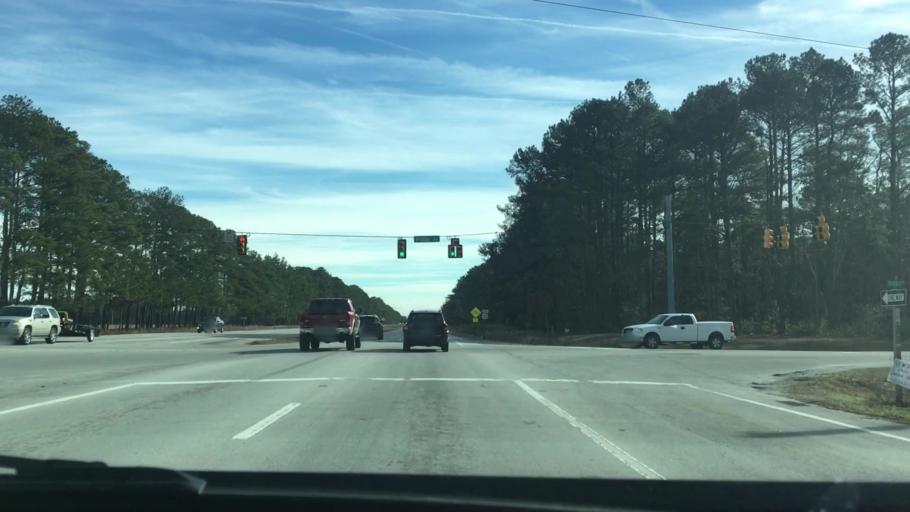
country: US
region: North Carolina
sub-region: Carteret County
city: Newport
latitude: 34.7706
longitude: -76.8654
